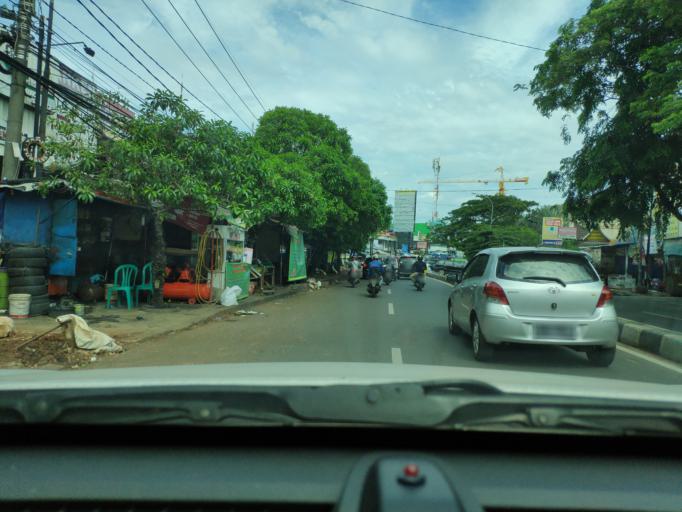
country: ID
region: West Java
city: Ciputat
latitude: -6.2247
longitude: 106.7100
